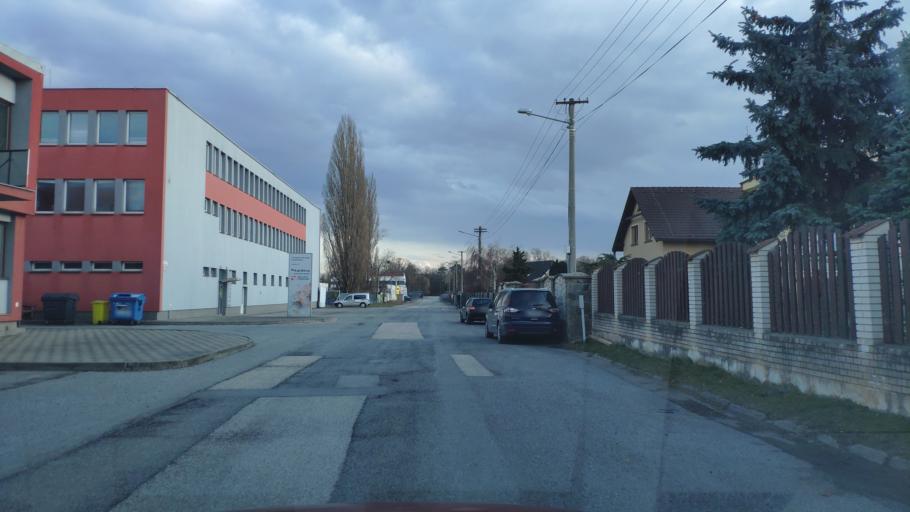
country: SK
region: Kosicky
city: Kosice
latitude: 48.6826
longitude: 21.2660
